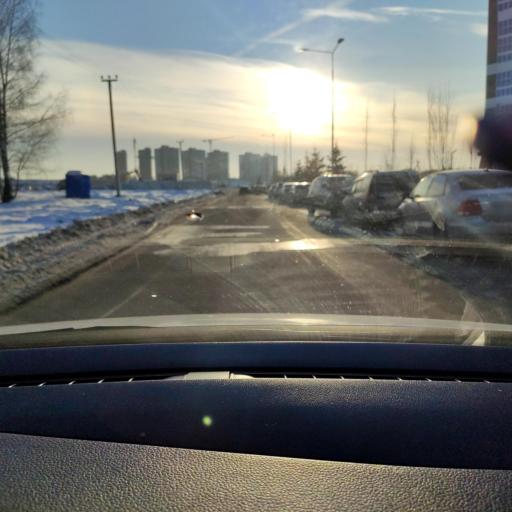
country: RU
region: Tatarstan
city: Stolbishchi
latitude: 55.6885
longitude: 49.2019
